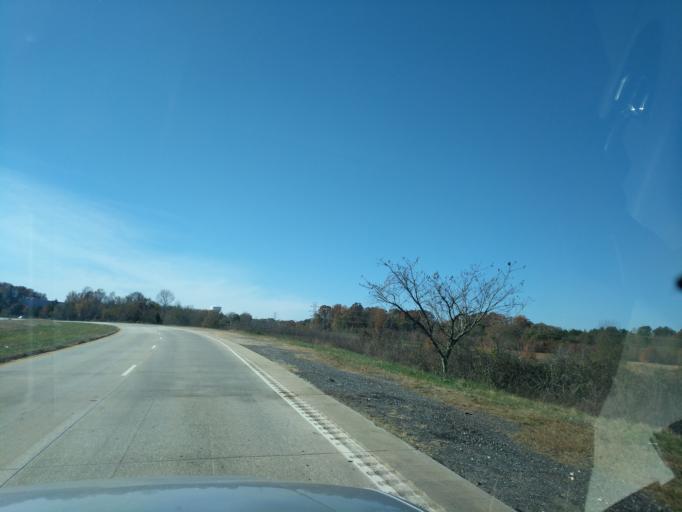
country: US
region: South Carolina
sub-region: Greenville County
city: Greer
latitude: 34.9103
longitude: -82.2160
